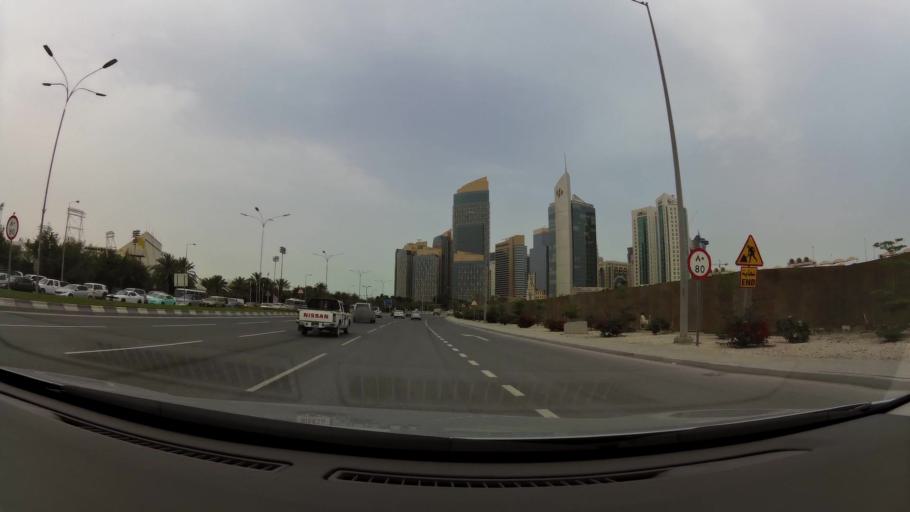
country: QA
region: Baladiyat ad Dawhah
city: Doha
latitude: 25.3108
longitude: 51.5154
